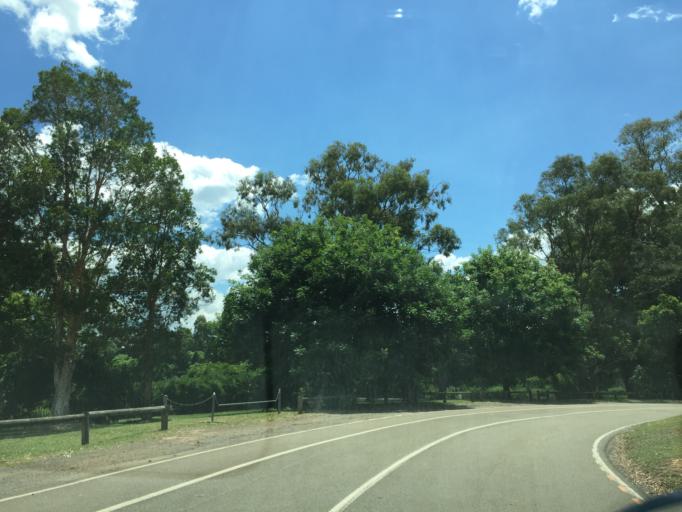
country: AU
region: New South Wales
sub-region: Parramatta
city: City of Parramatta
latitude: -33.8045
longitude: 150.9977
